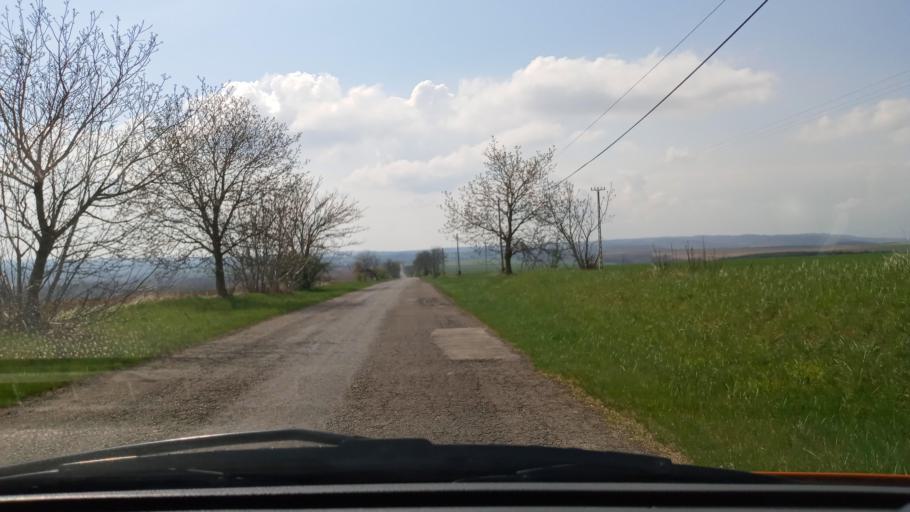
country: HU
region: Baranya
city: Pecsvarad
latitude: 46.1024
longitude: 18.4965
